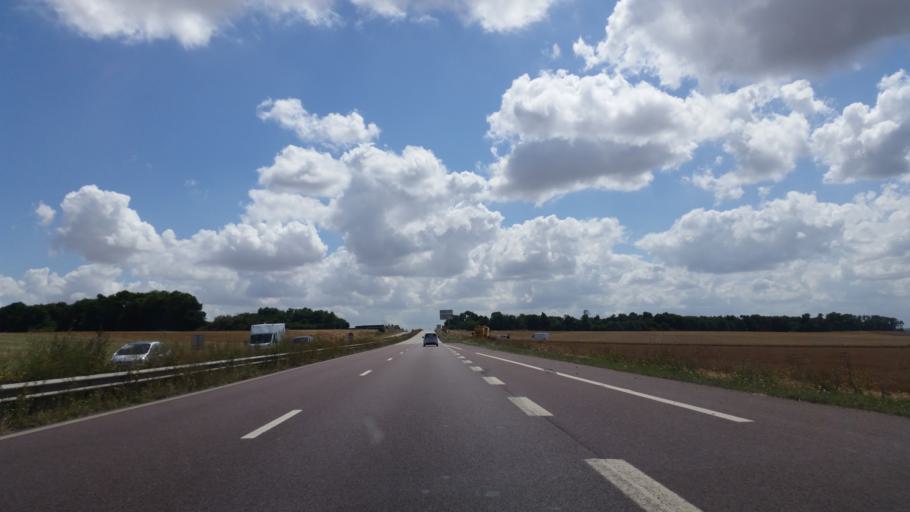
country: FR
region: Lower Normandy
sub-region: Departement du Calvados
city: Bourguebus
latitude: 49.0850
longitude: -0.3041
